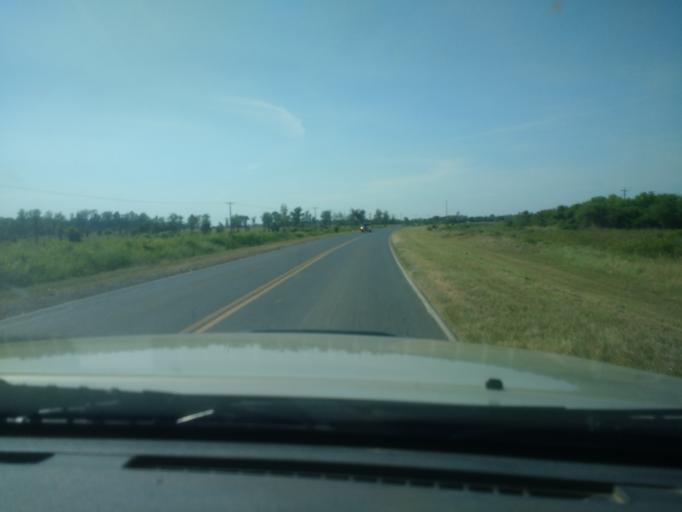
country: PY
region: Presidente Hayes
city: Benjamin Aceval
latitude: -24.9391
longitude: -57.5558
